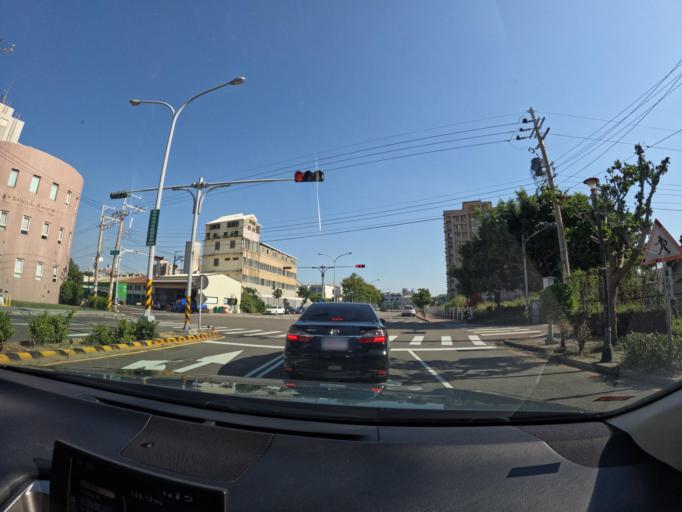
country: TW
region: Taiwan
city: Fengyuan
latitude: 24.2668
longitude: 120.5611
